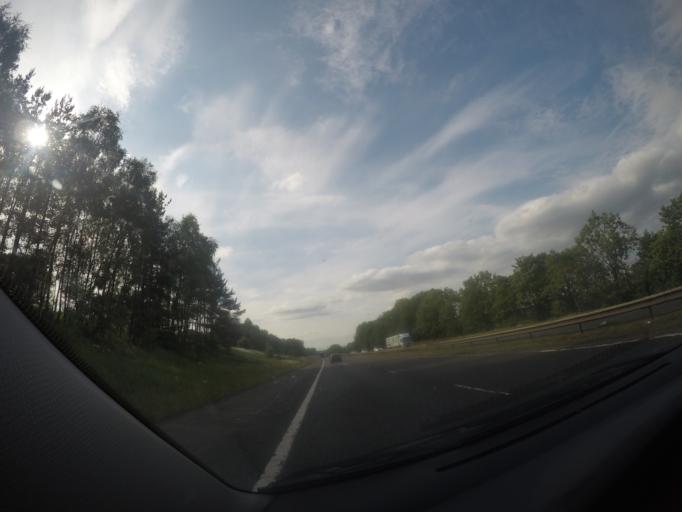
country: GB
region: Scotland
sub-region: South Lanarkshire
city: Larkhall
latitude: 55.7564
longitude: -3.9735
